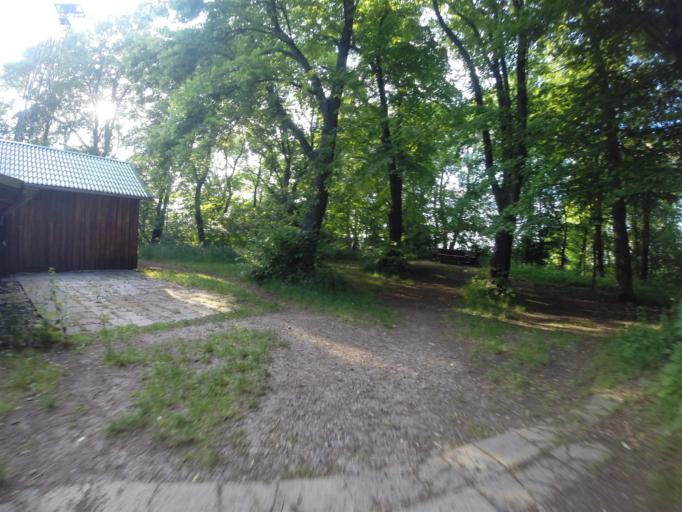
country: DE
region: Thuringia
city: Golmsdorf
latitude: 50.9599
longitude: 11.6489
